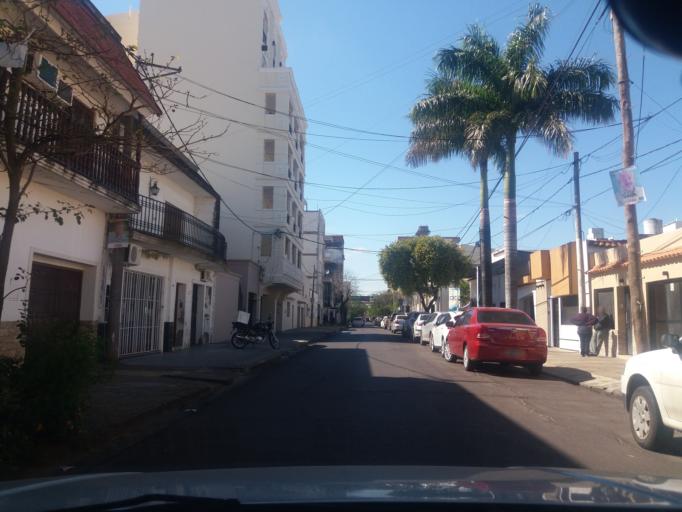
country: AR
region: Corrientes
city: Corrientes
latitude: -27.4725
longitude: -58.8457
